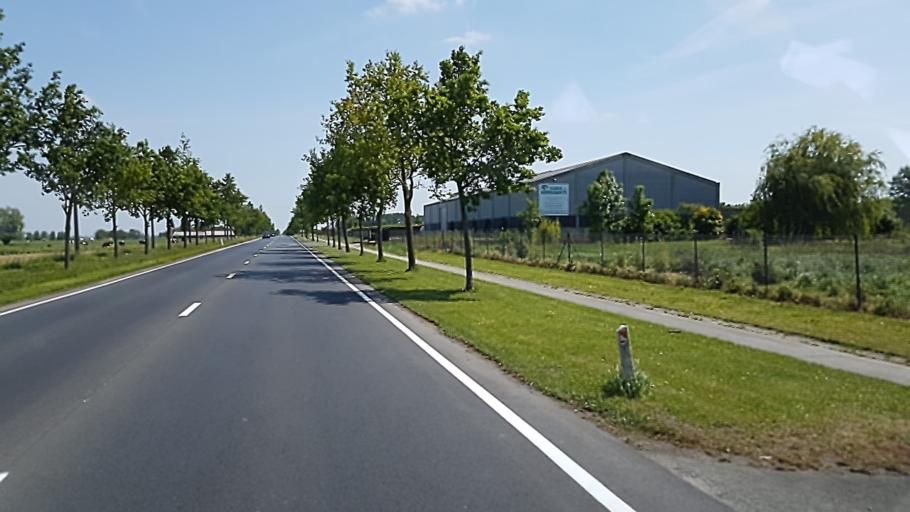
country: BE
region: Flanders
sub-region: Provincie West-Vlaanderen
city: Wervik
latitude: 50.8256
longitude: 3.0218
